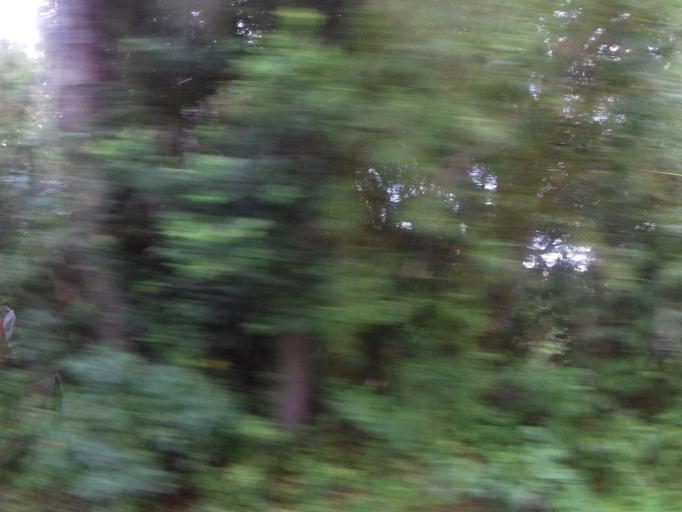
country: US
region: Florida
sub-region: Duval County
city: Jacksonville
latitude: 30.2969
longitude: -81.5992
